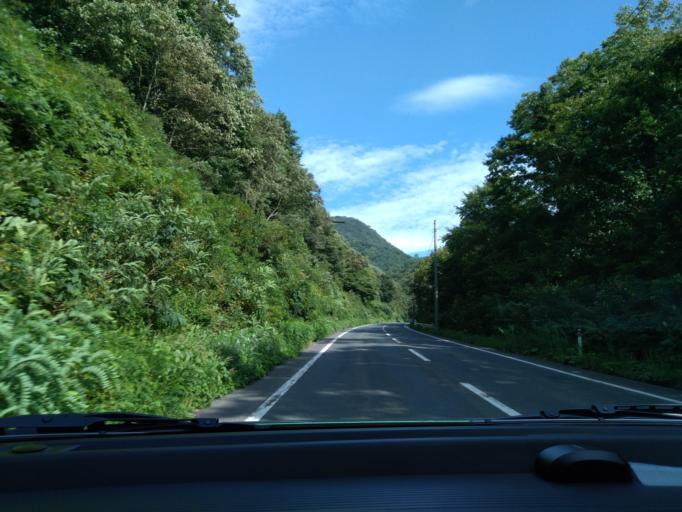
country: JP
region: Iwate
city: Shizukuishi
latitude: 39.6374
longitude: 141.0241
